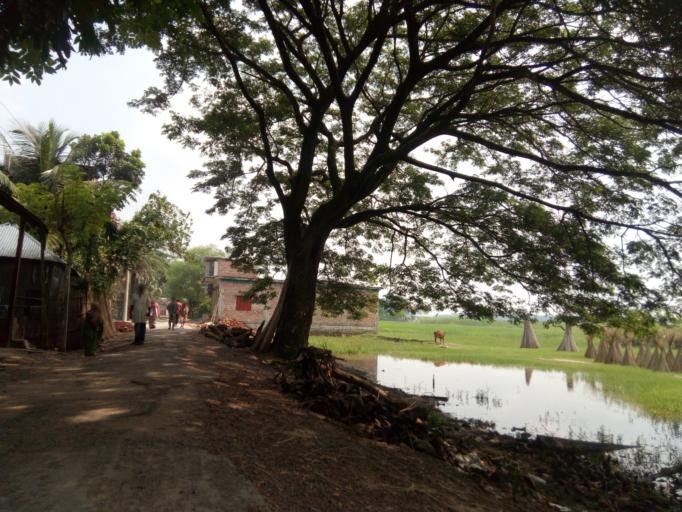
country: BD
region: Khulna
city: Kalia
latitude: 23.0817
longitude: 89.6680
